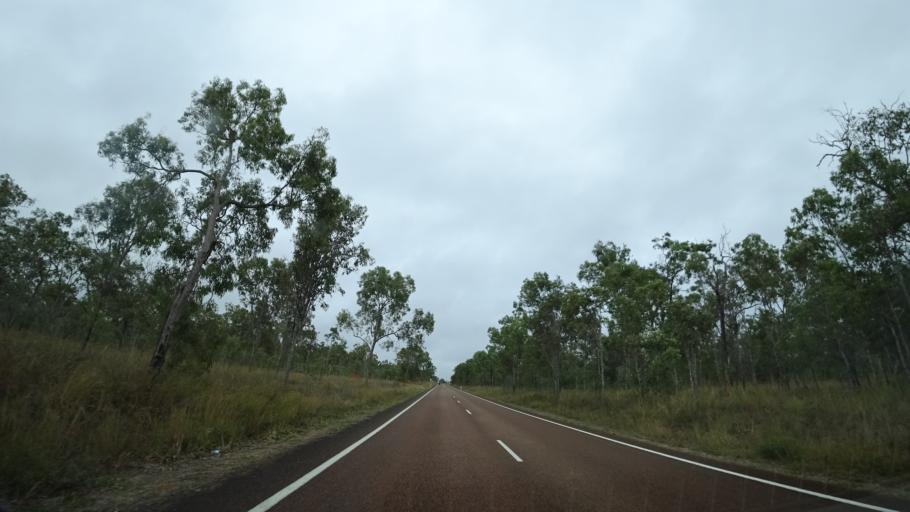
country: AU
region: Queensland
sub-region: Tablelands
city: Ravenshoe
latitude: -17.6806
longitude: 145.2344
